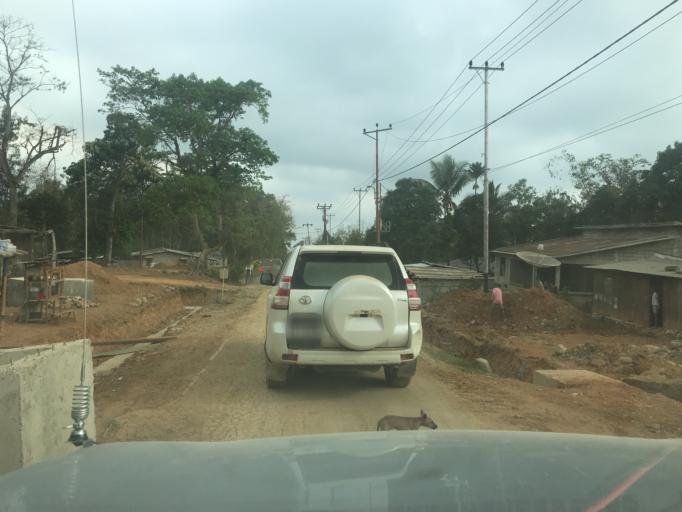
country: TL
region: Ainaro
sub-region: Ainaro
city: Ainaro
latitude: -9.0062
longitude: 125.5020
